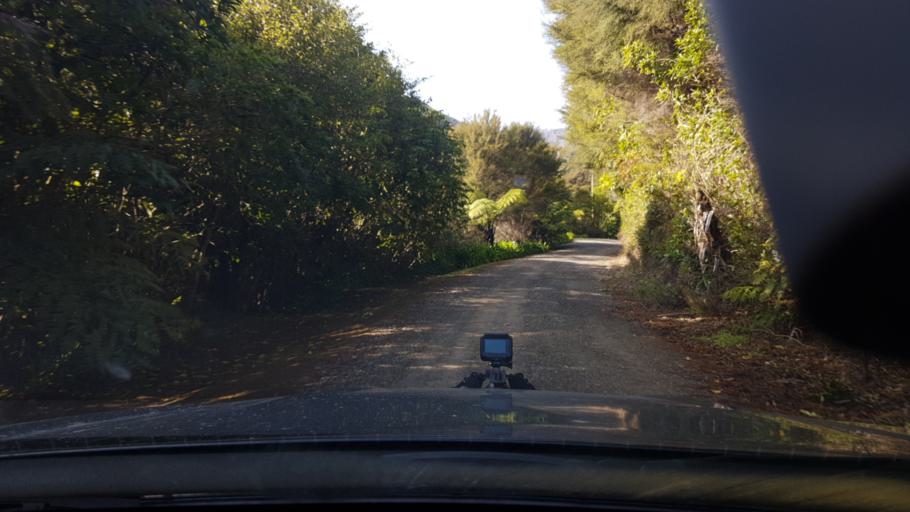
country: NZ
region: Marlborough
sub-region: Marlborough District
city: Picton
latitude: -41.2227
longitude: 173.9647
